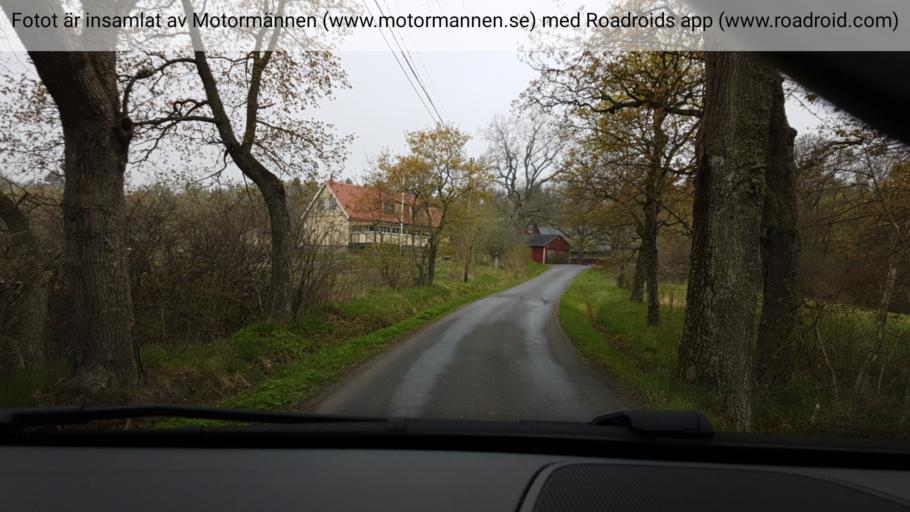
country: SE
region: Stockholm
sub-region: Haninge Kommun
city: Jordbro
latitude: 59.0138
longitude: 18.1152
